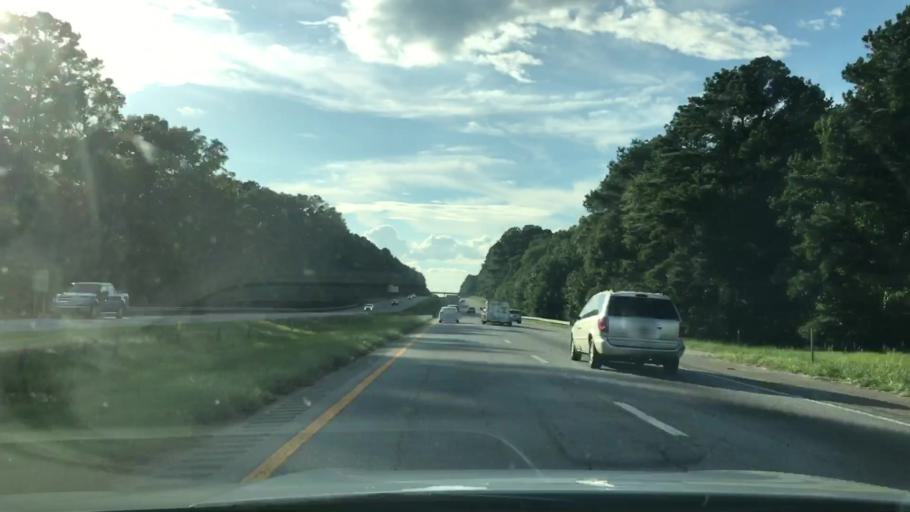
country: US
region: South Carolina
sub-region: Newberry County
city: Newberry
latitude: 34.3130
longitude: -81.5760
